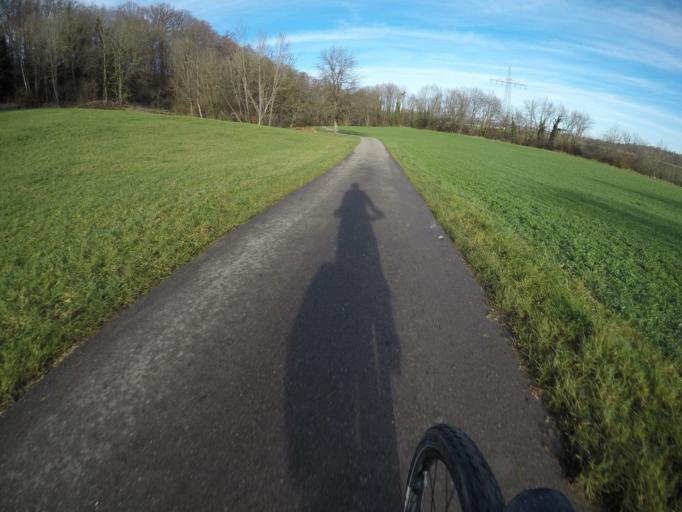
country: DE
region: Baden-Wuerttemberg
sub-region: Regierungsbezirk Stuttgart
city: Owen
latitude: 48.5992
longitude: 9.4432
